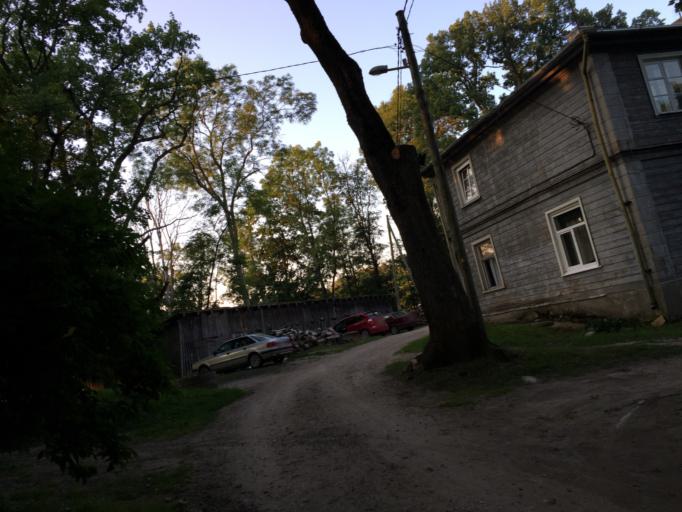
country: LV
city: Tervete
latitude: 56.4814
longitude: 23.3890
